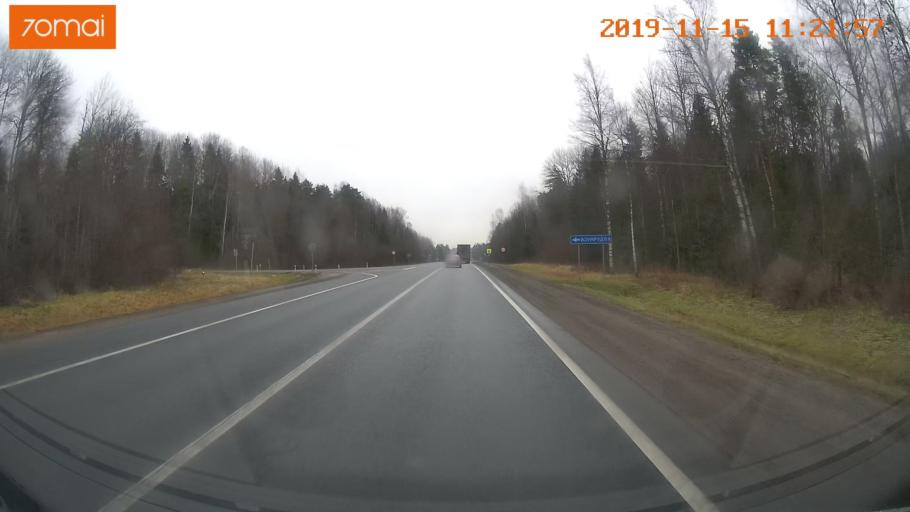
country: RU
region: Vologda
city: Molochnoye
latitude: 59.1462
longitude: 39.3509
